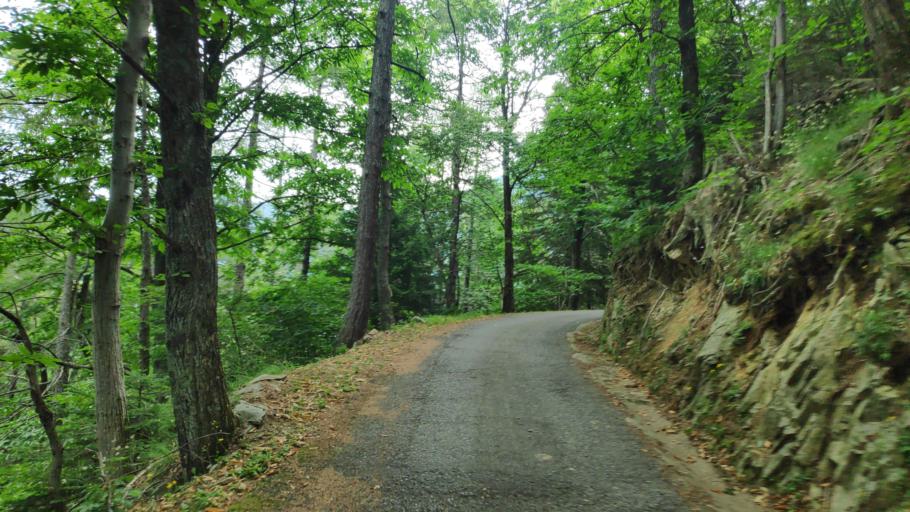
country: IT
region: Lombardy
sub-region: Provincia di Sondrio
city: Prata Camportaccio
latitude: 46.2937
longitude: 9.4107
